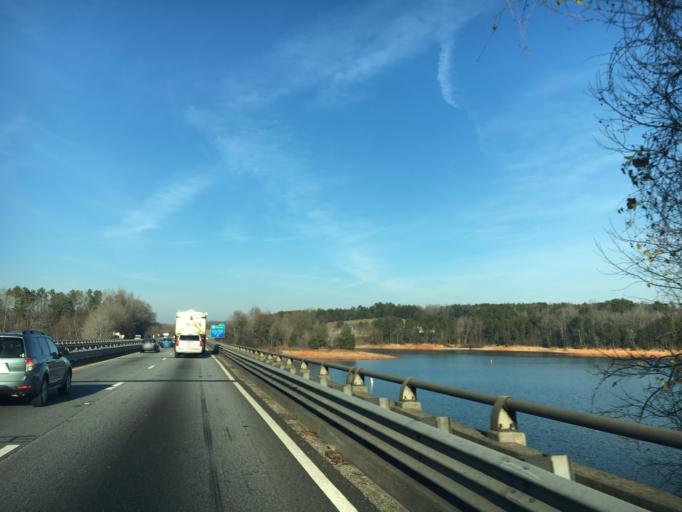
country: US
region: Georgia
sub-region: Franklin County
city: Gumlog
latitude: 34.4827
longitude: -83.0292
